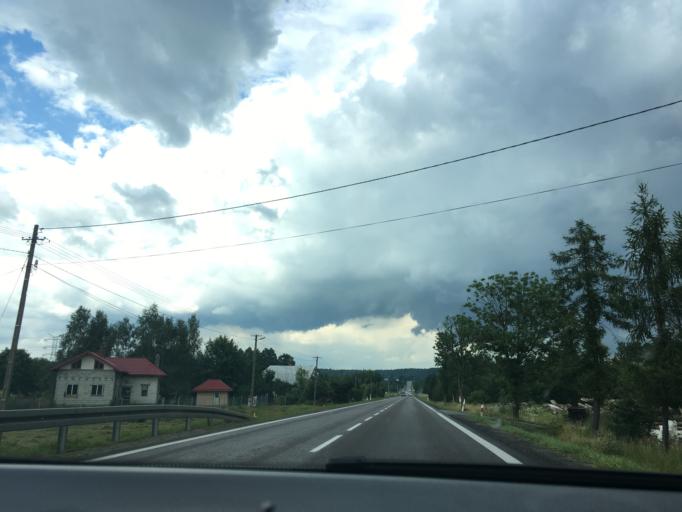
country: PL
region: Subcarpathian Voivodeship
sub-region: Powiat brzozowski
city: Jablonica Polska
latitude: 49.6946
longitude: 21.8728
